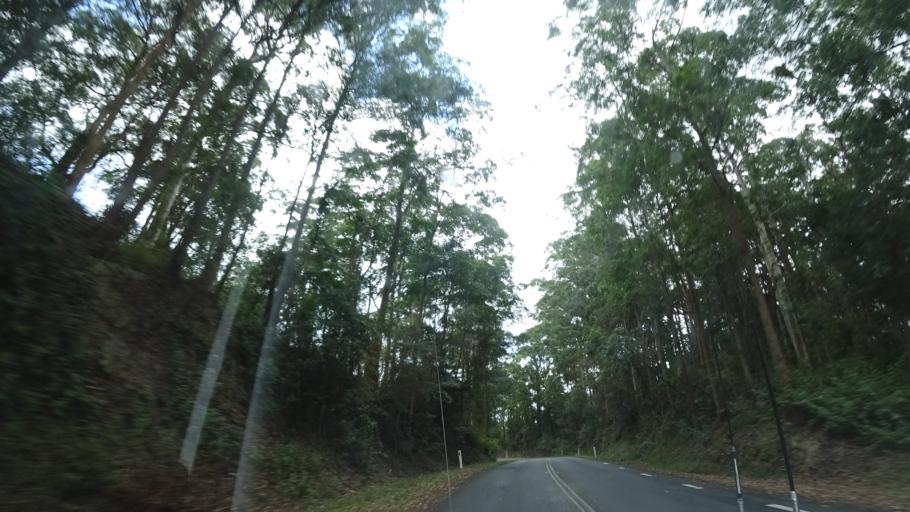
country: AU
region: Queensland
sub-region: Moreton Bay
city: Highvale
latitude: -27.3452
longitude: 152.7735
